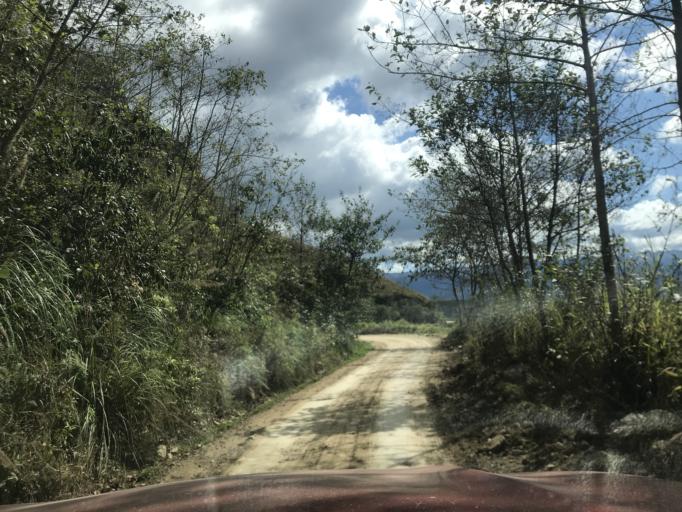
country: PE
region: Cajamarca
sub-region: Provincia de Chota
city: Querocoto
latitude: -6.3338
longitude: -79.0736
